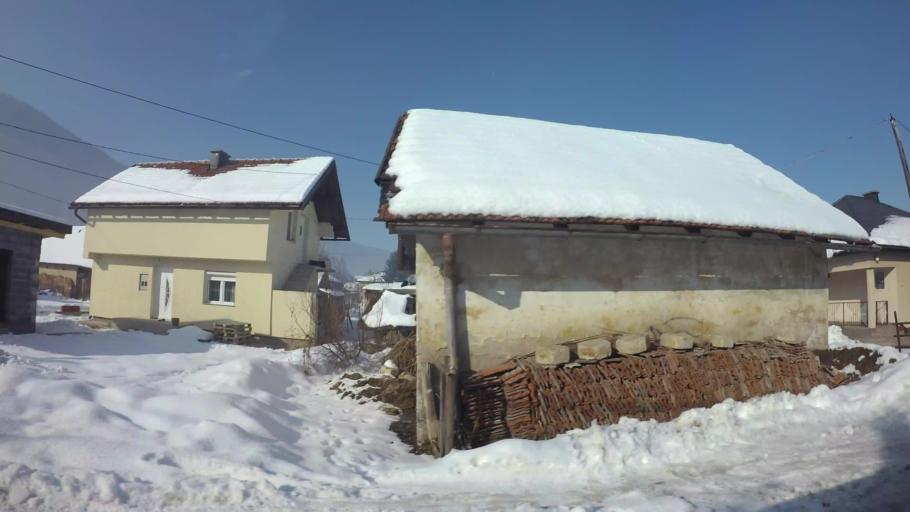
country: BA
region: Federation of Bosnia and Herzegovina
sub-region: Kanton Sarajevo
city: Sarajevo
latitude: 43.8031
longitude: 18.3025
